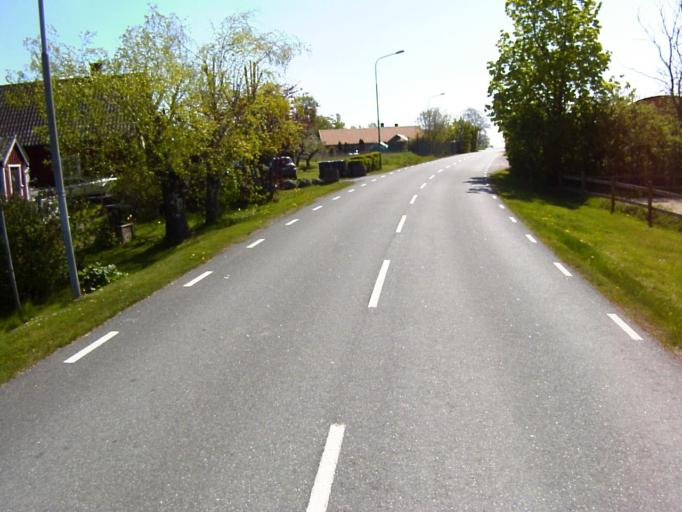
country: SE
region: Skane
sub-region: Kristianstads Kommun
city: Fjalkinge
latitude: 56.0104
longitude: 14.2435
